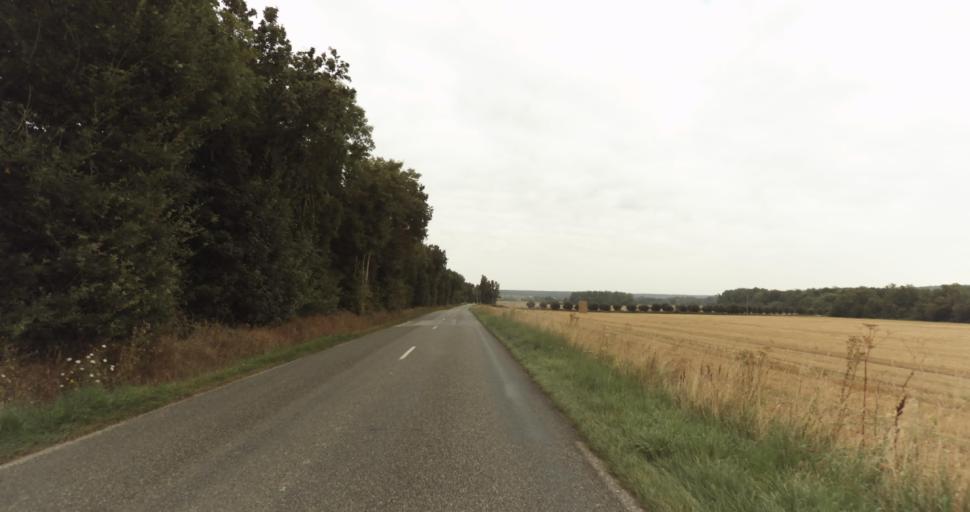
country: FR
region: Haute-Normandie
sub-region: Departement de l'Eure
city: Marcilly-sur-Eure
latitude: 48.8043
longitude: 1.3489
